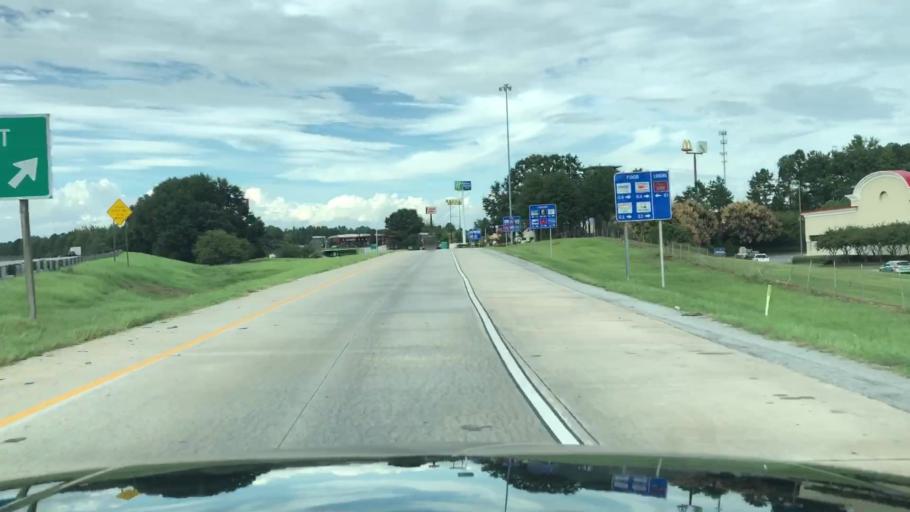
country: US
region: Georgia
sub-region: Henry County
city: Locust Grove
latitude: 33.3504
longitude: -84.1241
